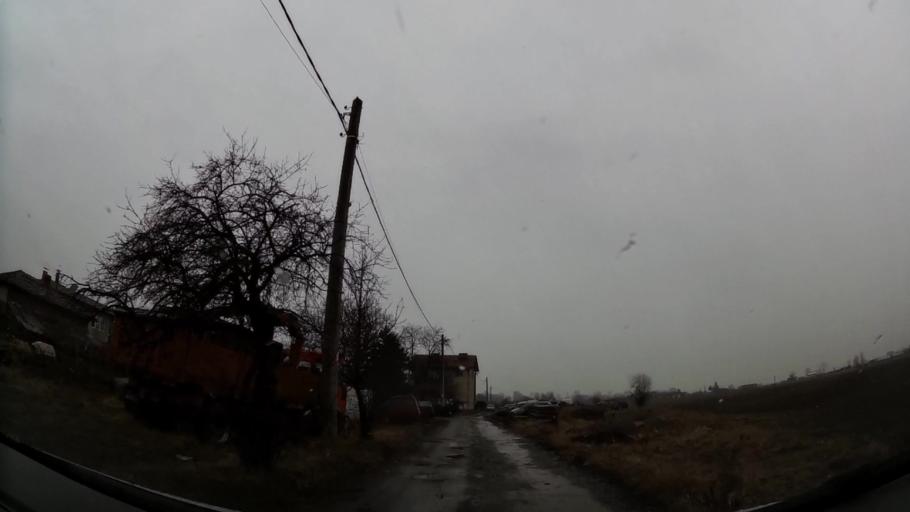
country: BG
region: Sofia-Capital
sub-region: Stolichna Obshtina
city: Sofia
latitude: 42.6660
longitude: 23.4272
